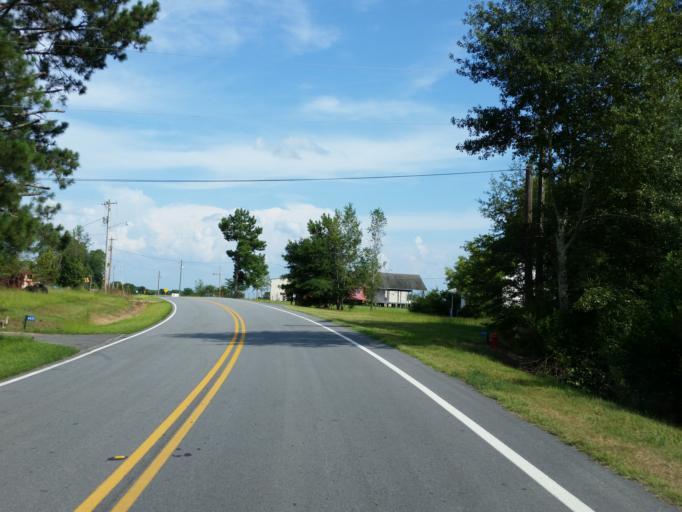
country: US
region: Georgia
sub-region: Crisp County
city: Cordele
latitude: 31.8272
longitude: -83.7393
